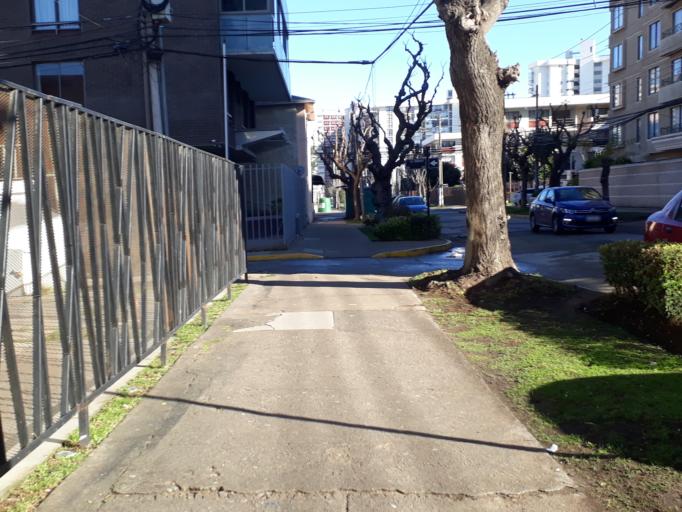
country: CL
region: Valparaiso
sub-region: Provincia de Valparaiso
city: Vina del Mar
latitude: -33.0132
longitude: -71.5501
